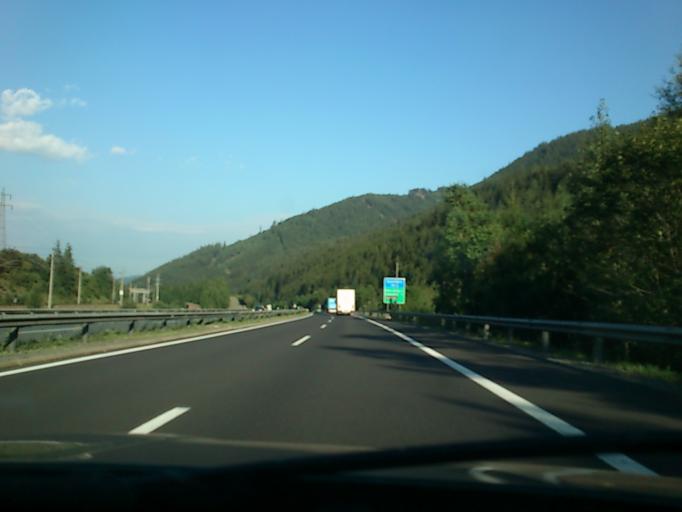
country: AT
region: Styria
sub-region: Politischer Bezirk Leoben
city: Kammern im Liesingtal
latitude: 47.3883
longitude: 14.8850
